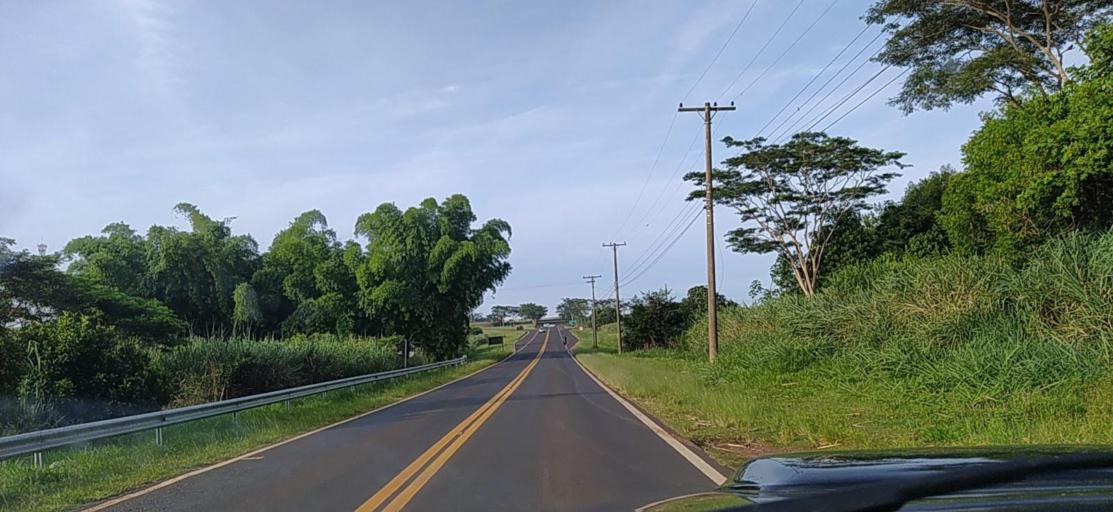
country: BR
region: Sao Paulo
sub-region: Pindorama
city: Pindorama
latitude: -21.2044
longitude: -48.9285
